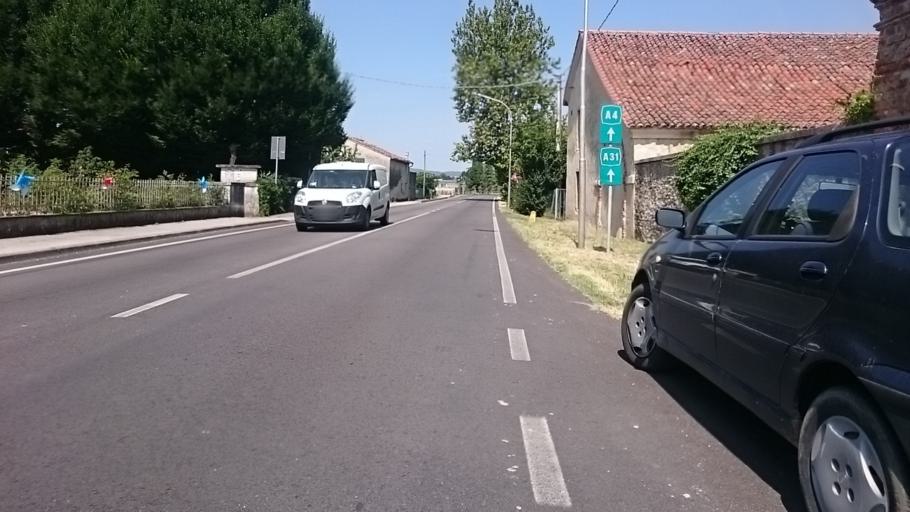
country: IT
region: Veneto
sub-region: Provincia di Padova
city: Cervarese Santa Croce
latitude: 45.4256
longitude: 11.6846
